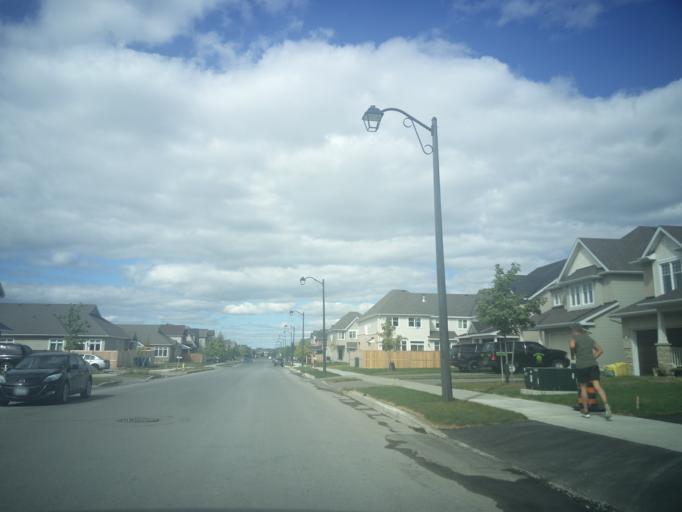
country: CA
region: Ontario
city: Bells Corners
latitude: 45.2480
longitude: -75.7389
